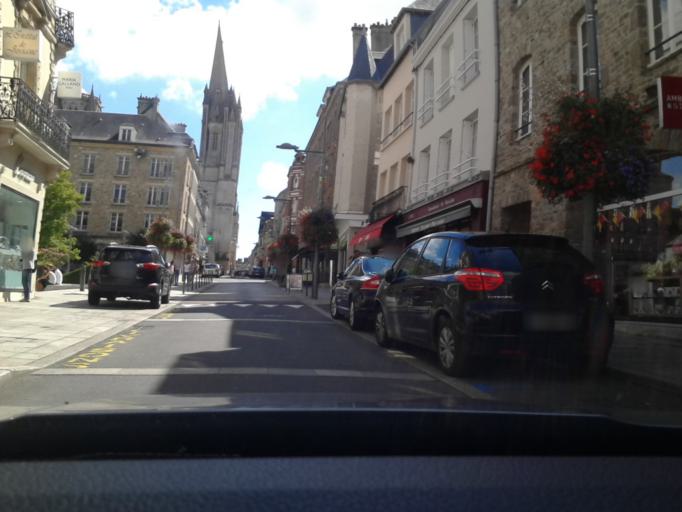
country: FR
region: Lower Normandy
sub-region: Departement de la Manche
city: Coutances
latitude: 49.0496
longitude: -1.4441
